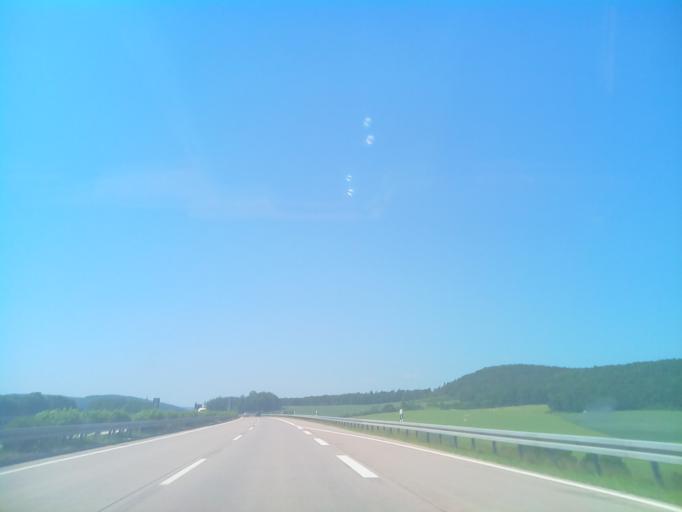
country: DE
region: Thuringia
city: Wolfershausen
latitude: 50.4740
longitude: 10.4525
